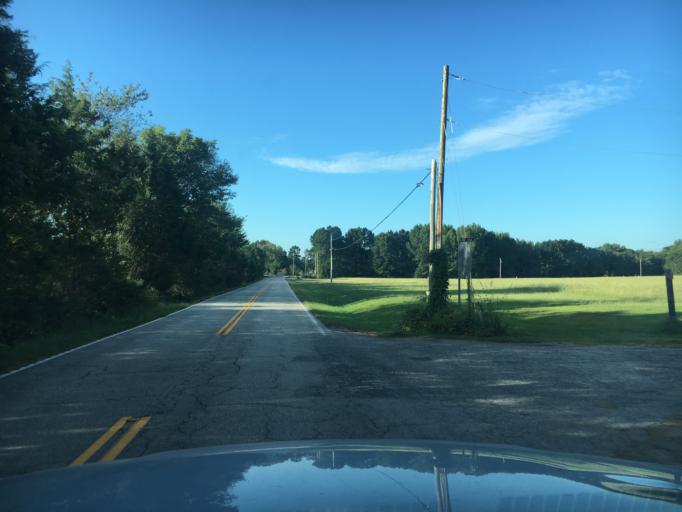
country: US
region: South Carolina
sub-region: Laurens County
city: Laurens
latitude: 34.5503
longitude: -82.0841
